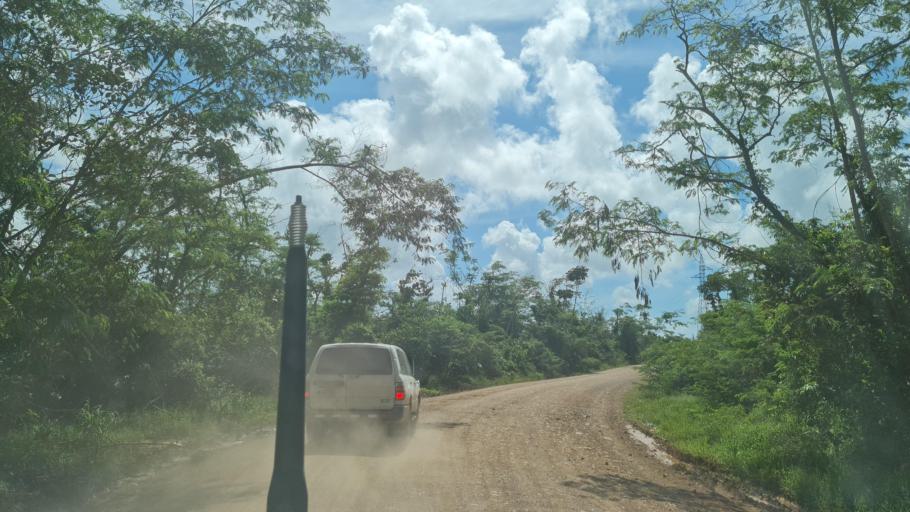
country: NI
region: Atlantico Norte (RAAN)
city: Puerto Cabezas
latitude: 14.1129
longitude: -83.5493
